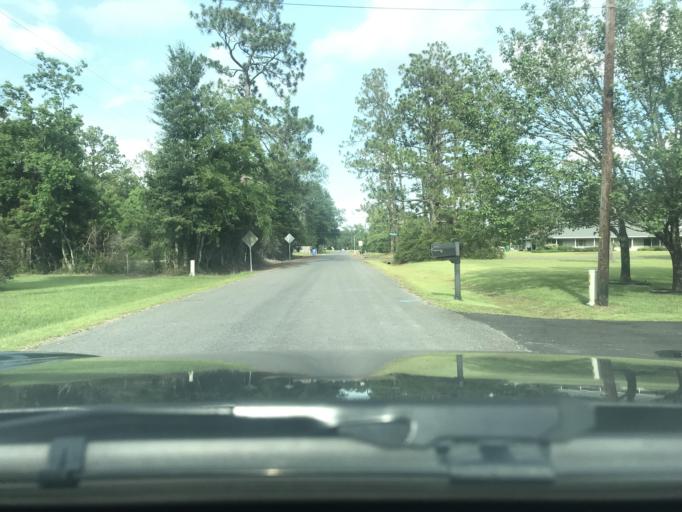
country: US
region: Louisiana
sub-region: Calcasieu Parish
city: Moss Bluff
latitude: 30.3371
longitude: -93.2621
